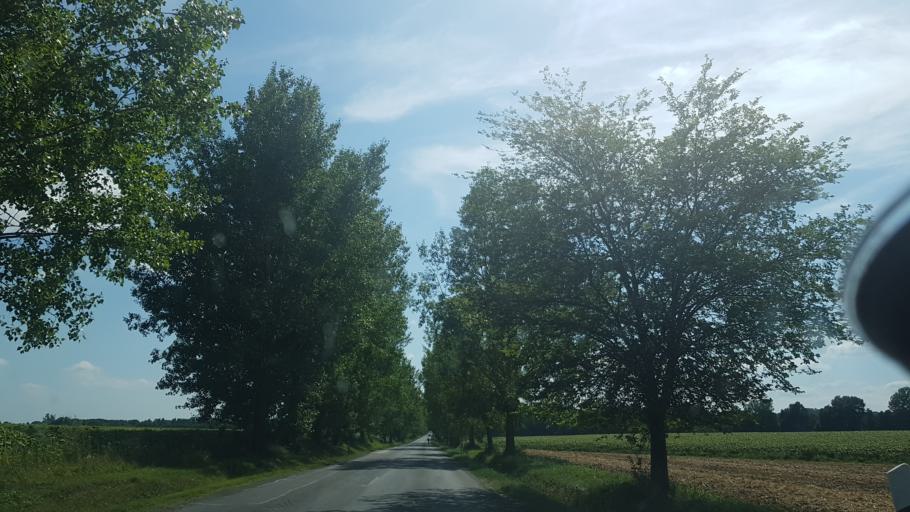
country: HU
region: Somogy
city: Segesd
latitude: 46.3774
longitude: 17.3649
